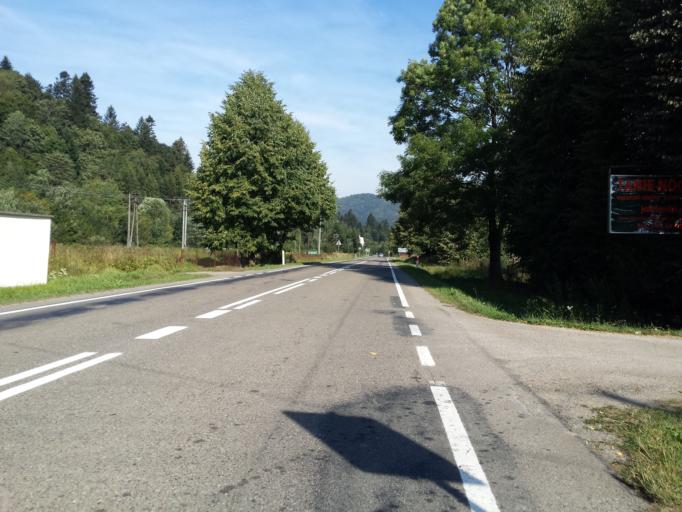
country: PL
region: Subcarpathian Voivodeship
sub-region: Powiat leski
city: Baligrod
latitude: 49.2778
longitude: 22.2827
